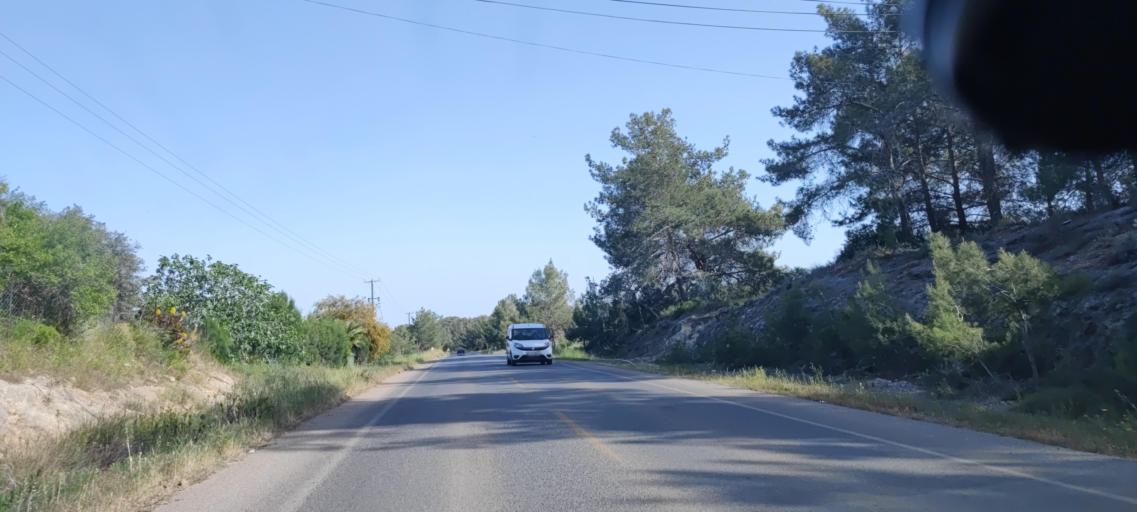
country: CY
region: Keryneia
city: Lapithos
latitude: 35.3116
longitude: 33.0585
